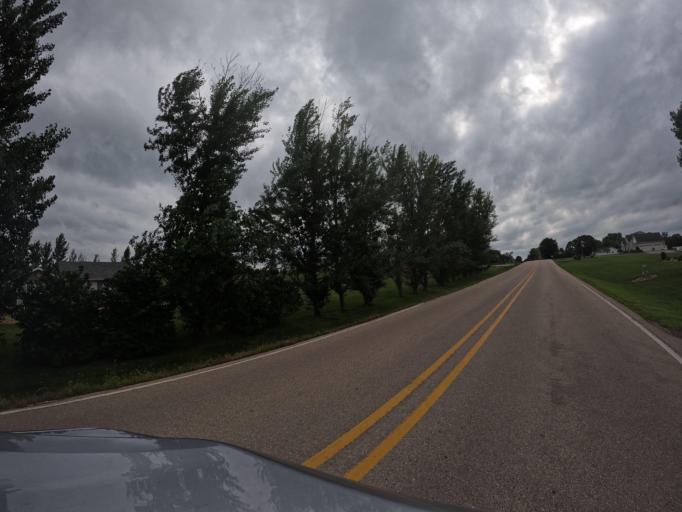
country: US
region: Iowa
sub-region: Clinton County
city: De Witt
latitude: 41.8004
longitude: -90.5407
